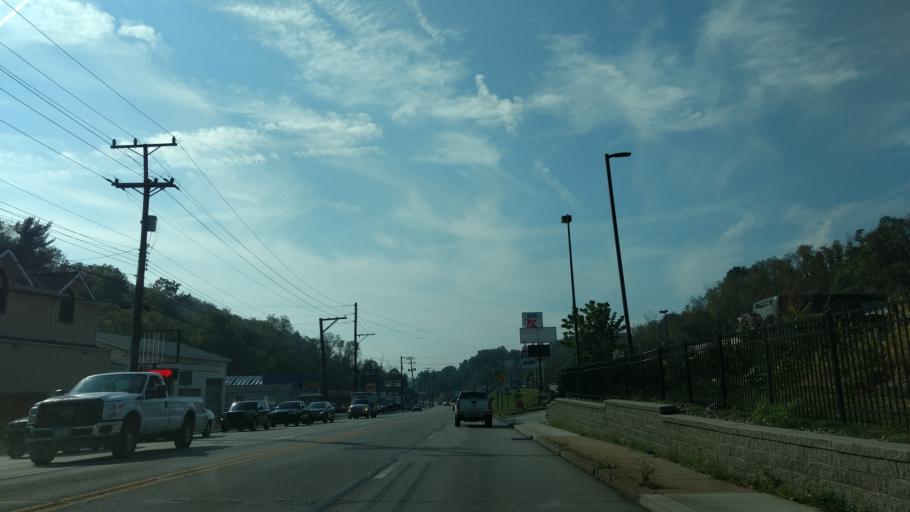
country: US
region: Pennsylvania
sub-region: Allegheny County
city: Pleasant Hills
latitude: 40.3283
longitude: -79.9449
